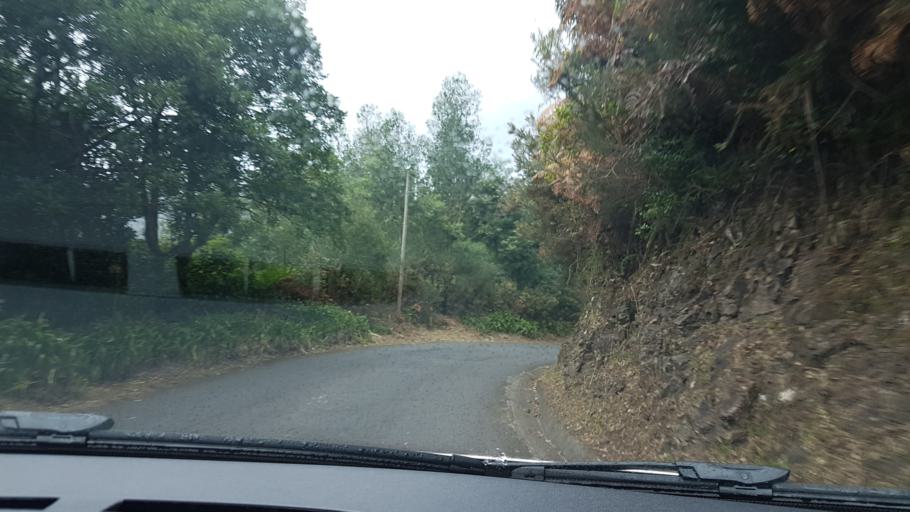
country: PT
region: Madeira
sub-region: Santa Cruz
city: Santa Cruz
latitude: 32.7276
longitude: -16.8119
